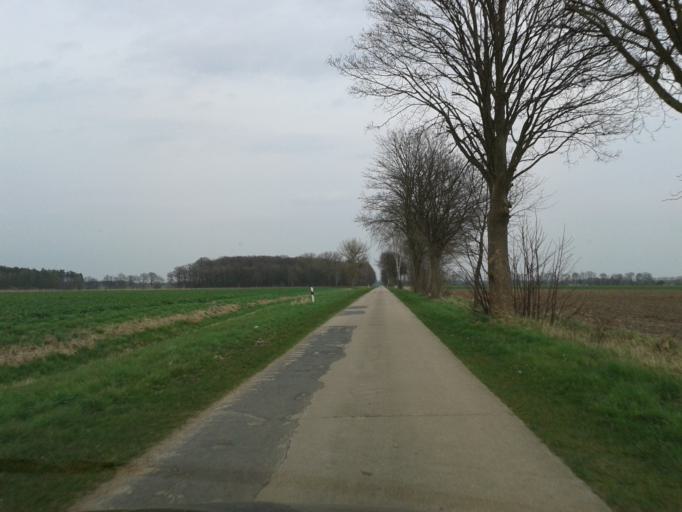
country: DE
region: Lower Saxony
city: Lubbow
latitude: 52.9077
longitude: 11.2066
